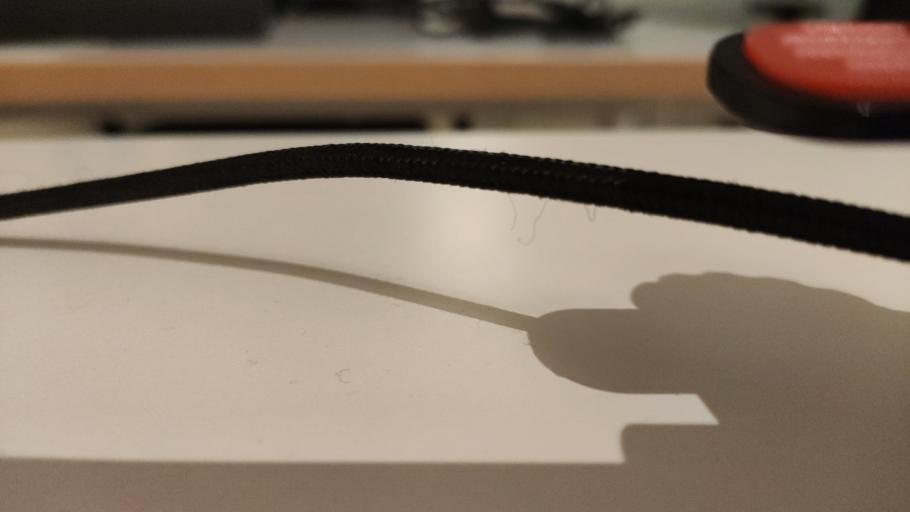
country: RU
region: Moskovskaya
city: Rybnoye
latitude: 56.4013
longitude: 37.6405
